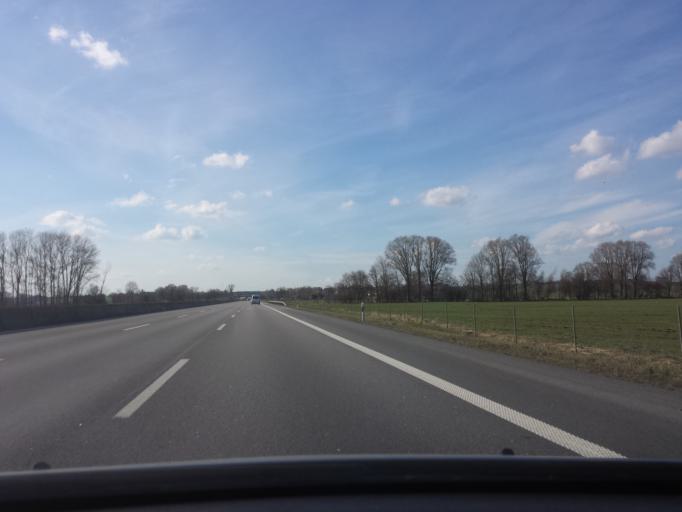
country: DE
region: Bavaria
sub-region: Upper Bavaria
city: Bergkirchen
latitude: 48.2444
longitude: 11.3280
